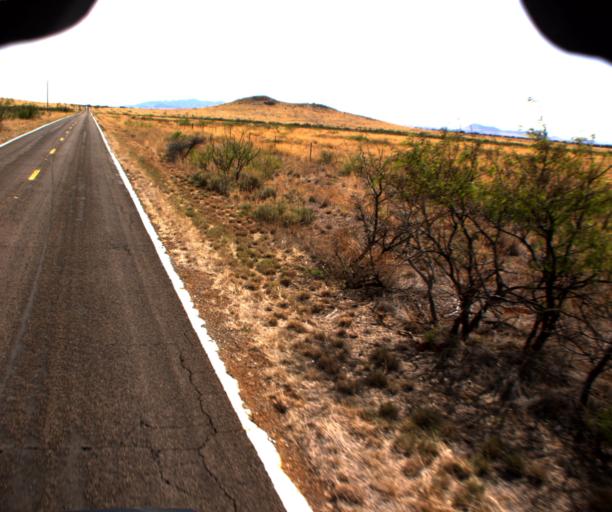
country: US
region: Arizona
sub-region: Cochise County
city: Willcox
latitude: 31.9630
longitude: -109.4771
